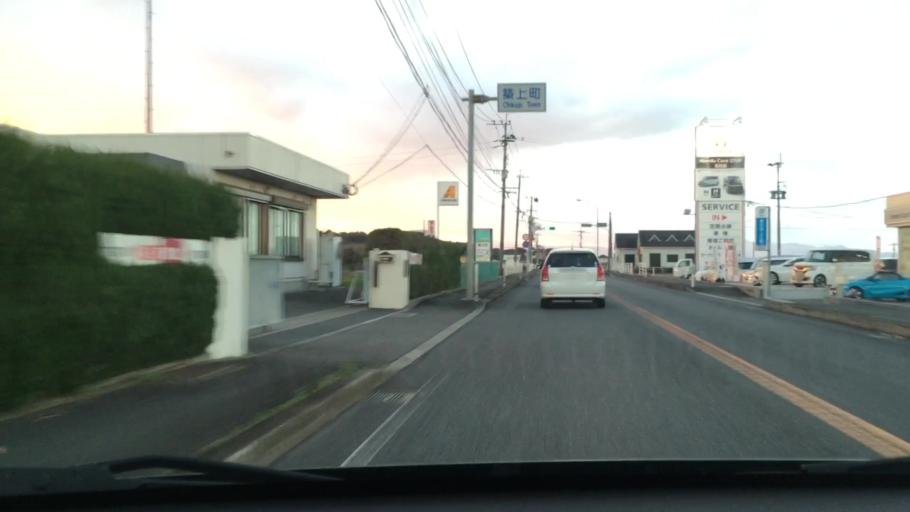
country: JP
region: Fukuoka
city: Shiida
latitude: 33.6298
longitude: 131.0851
